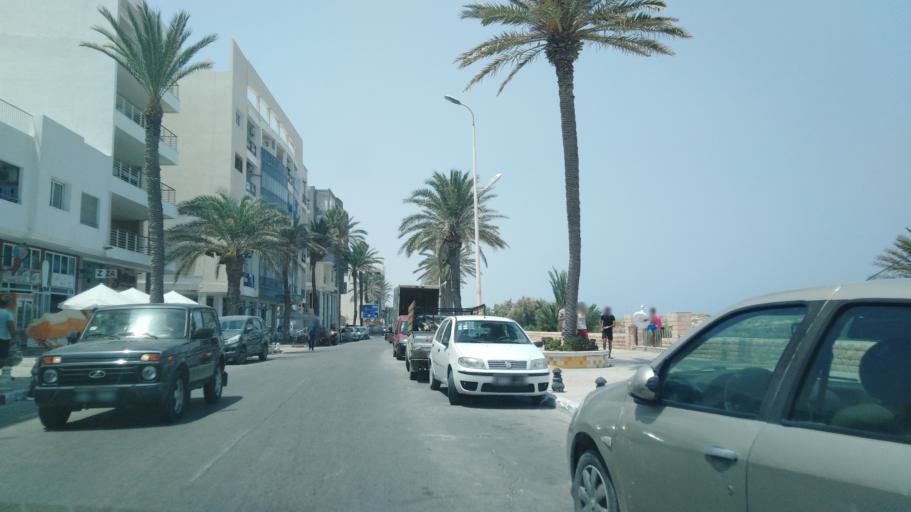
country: TN
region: Al Mahdiyah
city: Mahdia
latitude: 35.5099
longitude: 11.0543
